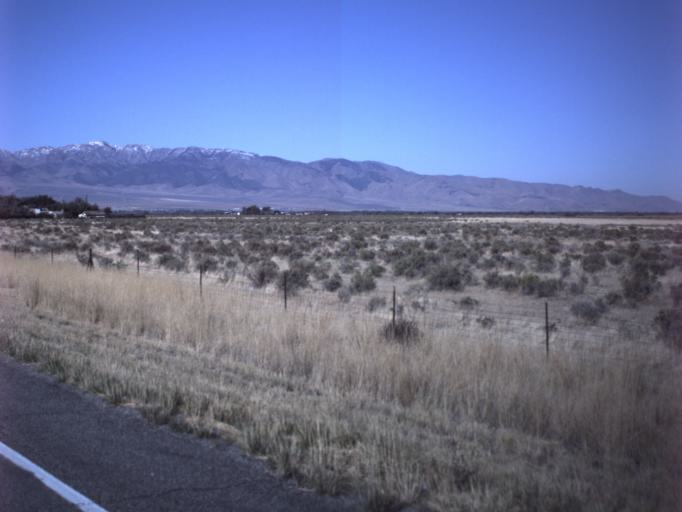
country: US
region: Utah
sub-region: Tooele County
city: Grantsville
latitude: 40.6061
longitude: -112.3878
